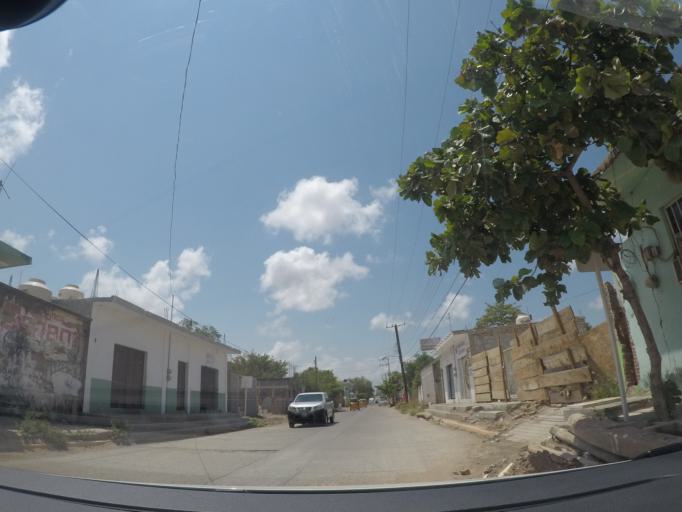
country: MX
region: Oaxaca
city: Juchitan de Zaragoza
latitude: 16.4360
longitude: -95.0177
